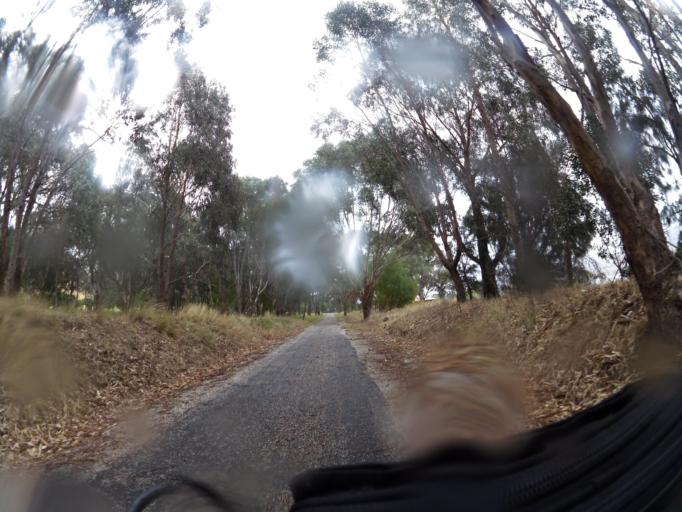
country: AU
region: New South Wales
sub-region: Albury Municipality
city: East Albury
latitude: -36.2164
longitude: 147.1931
